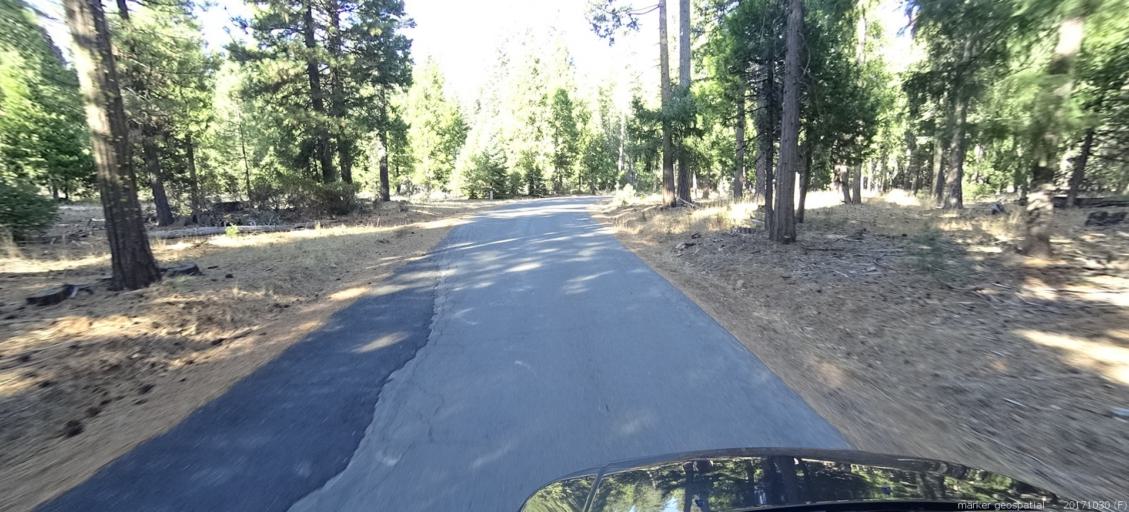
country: US
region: California
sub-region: Shasta County
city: Shingletown
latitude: 40.5497
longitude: -121.7339
